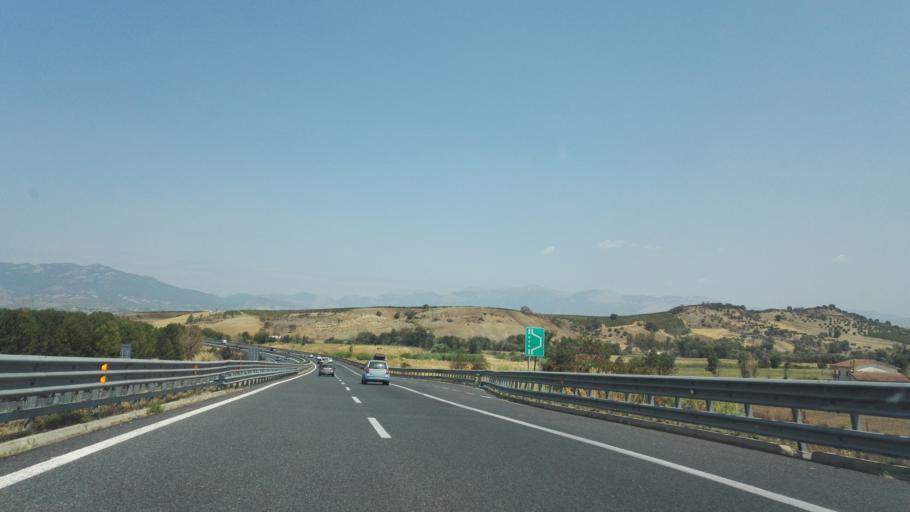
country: IT
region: Calabria
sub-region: Provincia di Cosenza
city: Tarsia
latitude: 39.6386
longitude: 16.2309
